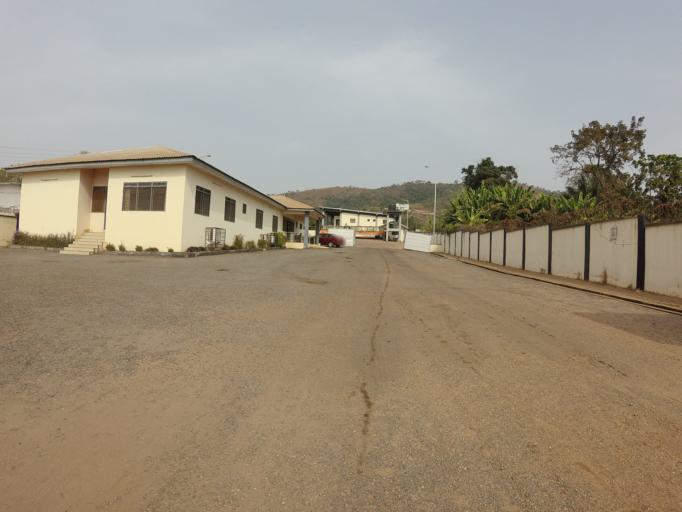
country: GH
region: Volta
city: Ho
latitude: 6.5988
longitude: 0.4470
